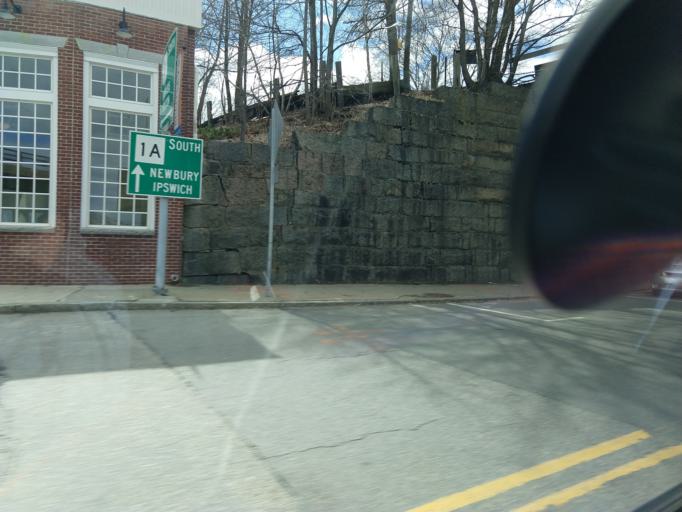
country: US
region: Massachusetts
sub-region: Essex County
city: Newburyport
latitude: 42.8129
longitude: -70.8755
